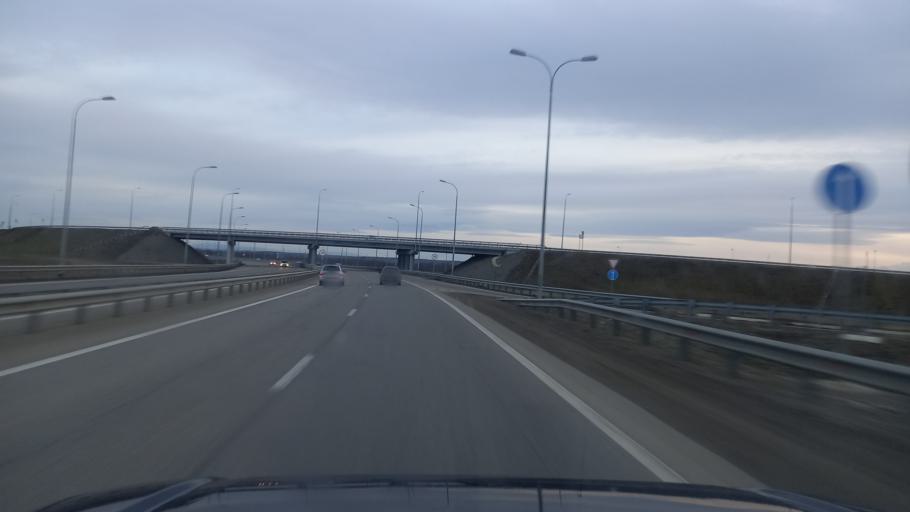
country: RU
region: Adygeya
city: Khanskaya
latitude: 44.6612
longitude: 39.9938
